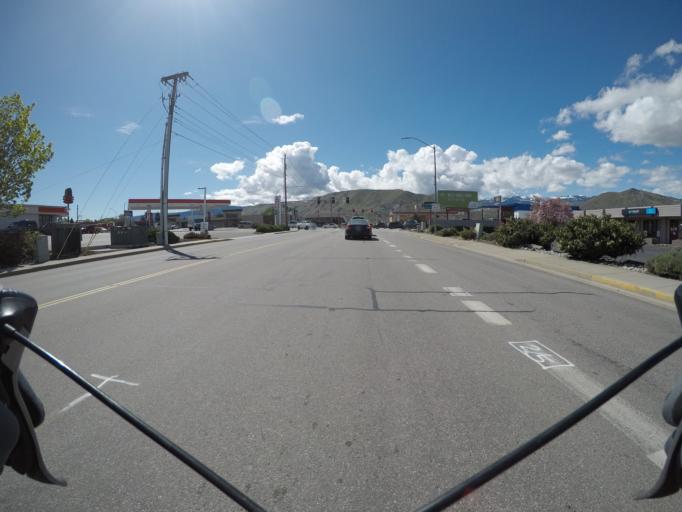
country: US
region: Washington
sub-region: Douglas County
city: East Wenatchee
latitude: 47.4068
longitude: -120.2885
